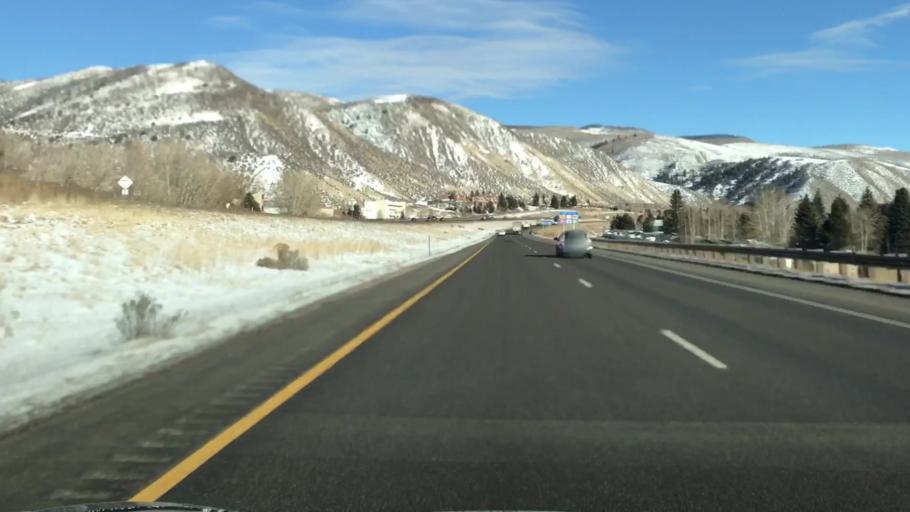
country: US
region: Colorado
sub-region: Eagle County
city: Avon
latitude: 39.6385
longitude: -106.5411
